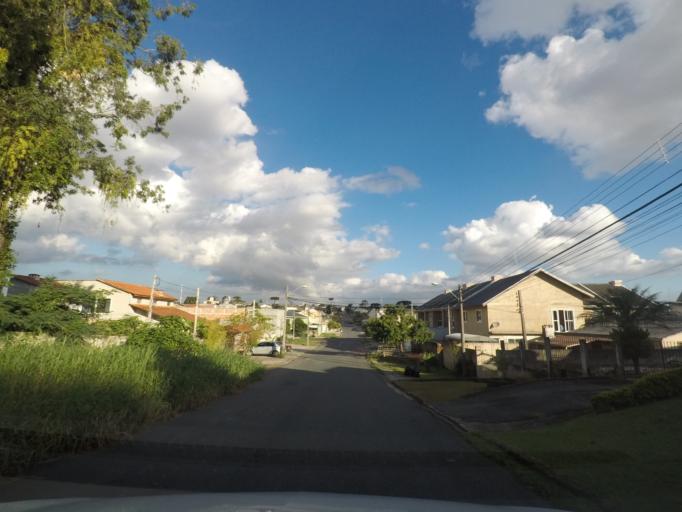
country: BR
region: Parana
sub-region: Sao Jose Dos Pinhais
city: Sao Jose dos Pinhais
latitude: -25.4946
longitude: -49.2562
